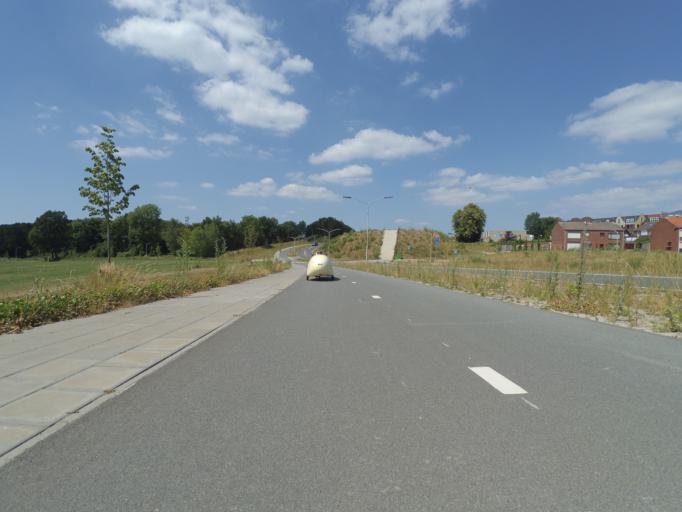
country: NL
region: North Brabant
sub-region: Gemeente Woensdrecht
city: Woensdrecht
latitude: 51.4242
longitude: 4.3196
